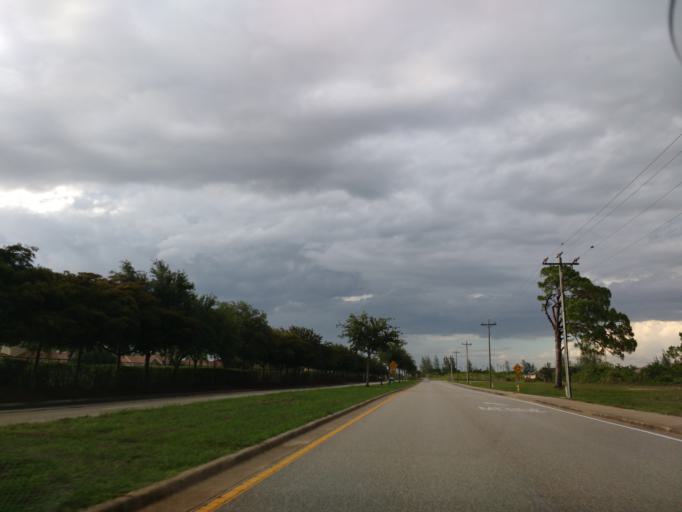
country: US
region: Florida
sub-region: Lee County
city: Cape Coral
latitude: 26.6198
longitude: -82.0232
